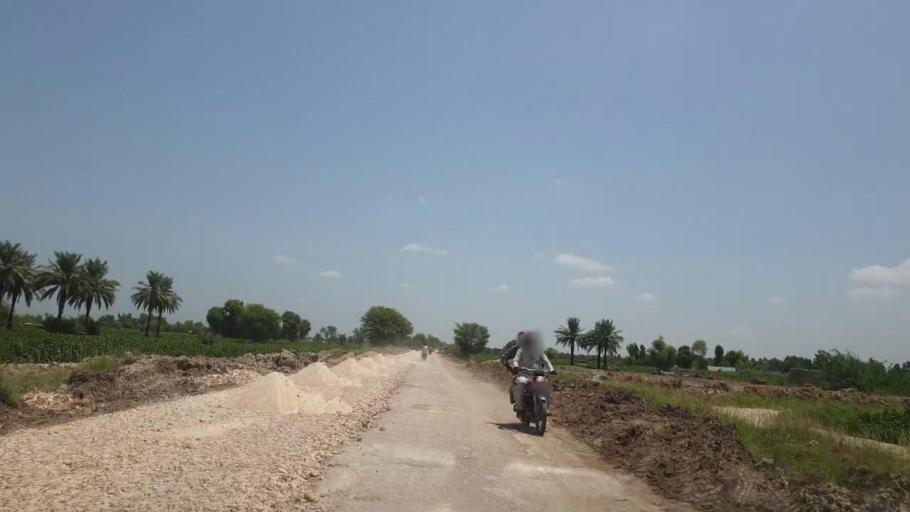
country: PK
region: Sindh
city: Pano Aqil
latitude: 27.6660
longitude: 69.1778
